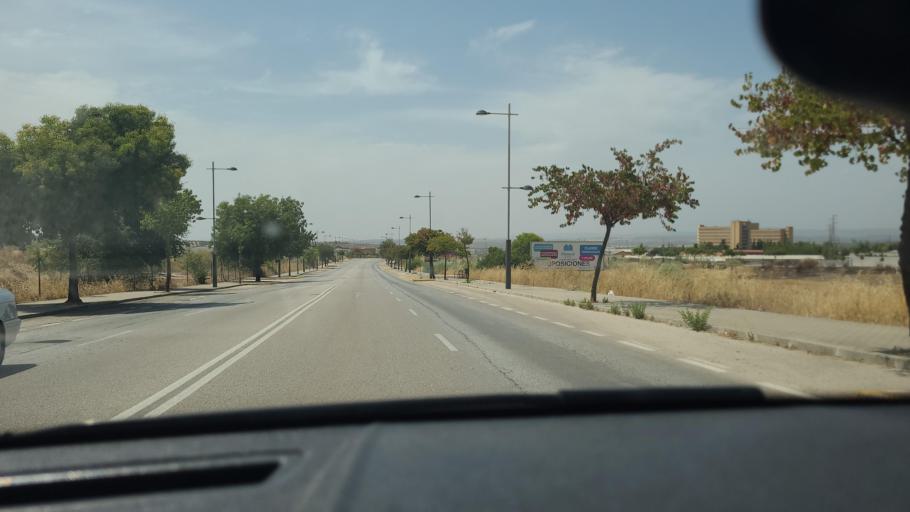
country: ES
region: Andalusia
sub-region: Provincia de Jaen
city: Linares
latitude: 38.0861
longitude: -3.6348
